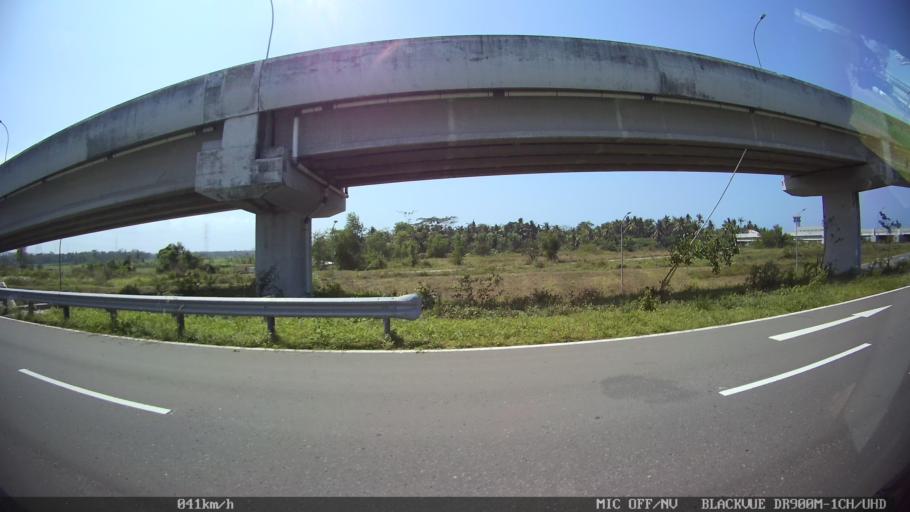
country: ID
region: Daerah Istimewa Yogyakarta
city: Srandakan
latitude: -7.8962
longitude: 110.0637
